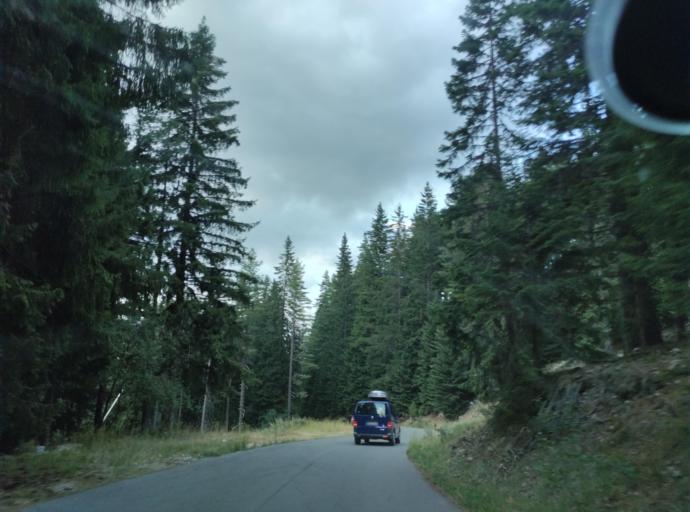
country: BG
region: Blagoevgrad
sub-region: Obshtina Bansko
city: Bansko
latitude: 41.7748
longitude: 23.4367
